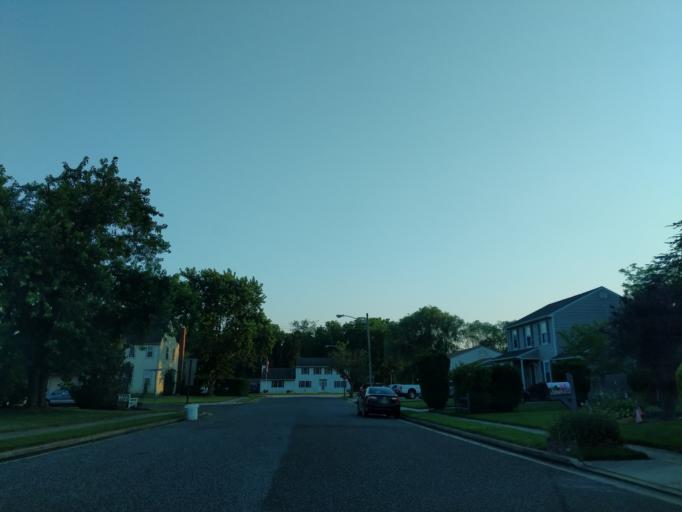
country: US
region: New Jersey
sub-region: Camden County
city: Glendora
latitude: 39.8126
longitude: -75.1023
